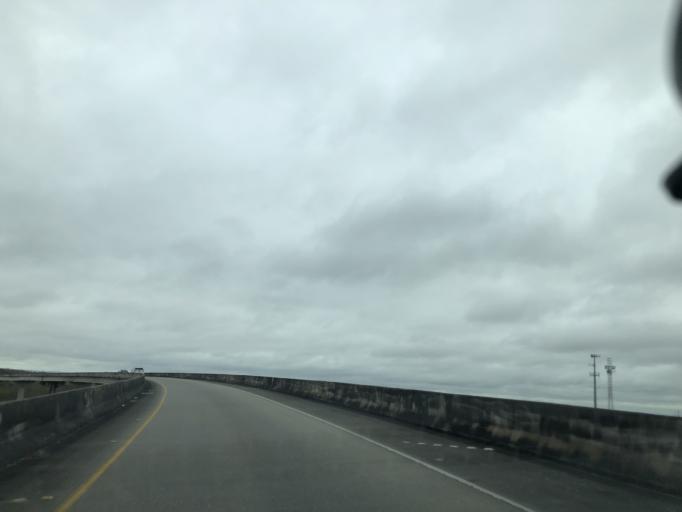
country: US
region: Louisiana
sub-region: Saint Charles Parish
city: Saint Rose
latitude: 29.9744
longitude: -90.3194
